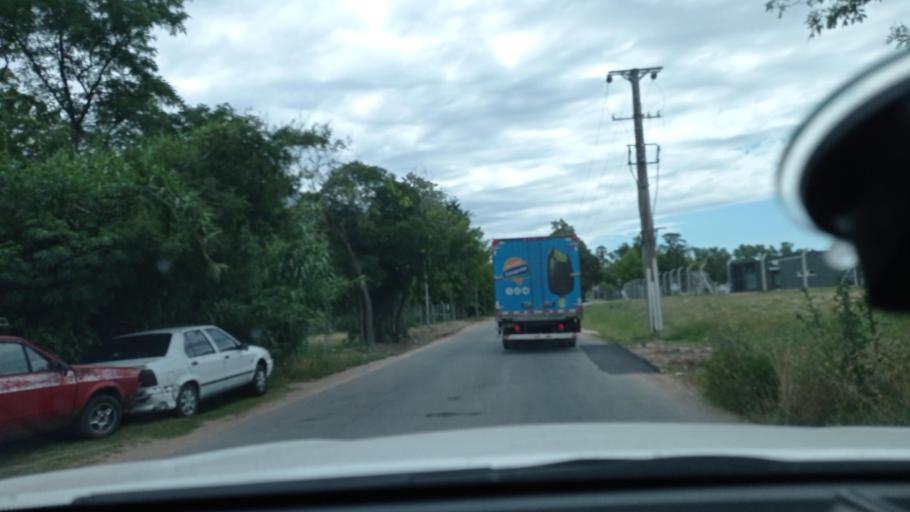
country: UY
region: Canelones
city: La Paz
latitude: -34.8089
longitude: -56.1914
